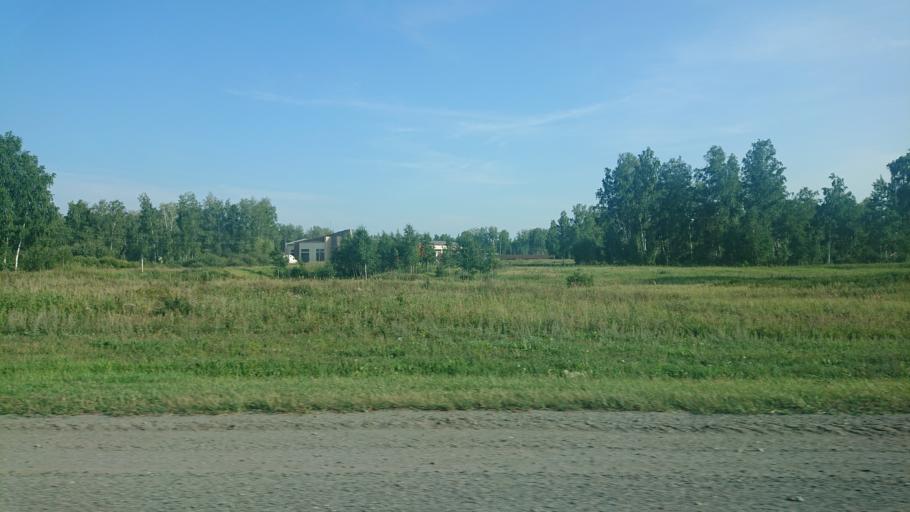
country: RU
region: Chelyabinsk
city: Vakhrushevo
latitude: 55.2496
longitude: 61.7982
